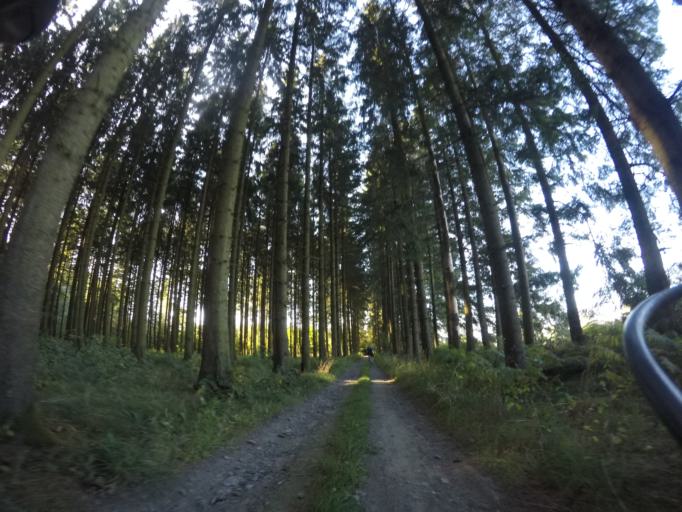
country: BE
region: Wallonia
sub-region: Province du Luxembourg
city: Bastogne
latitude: 49.9701
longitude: 5.6898
